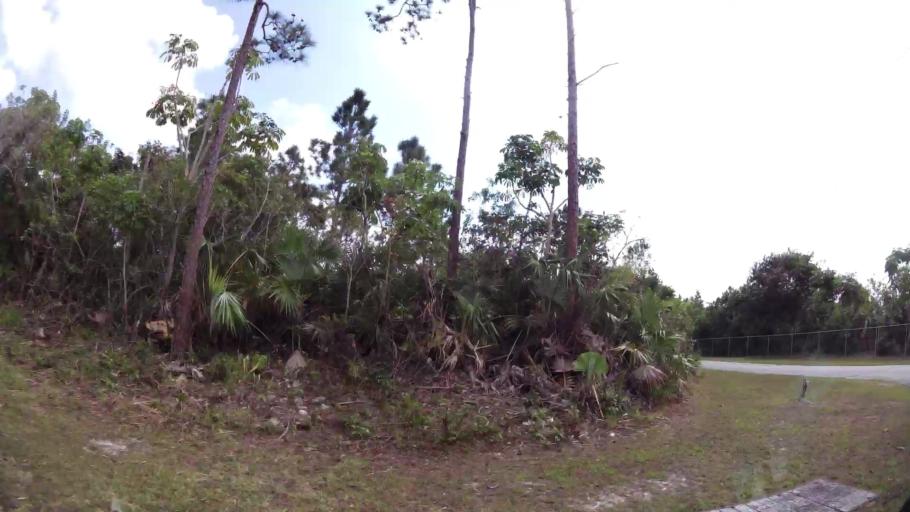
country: BS
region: Freeport
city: Freeport
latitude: 26.5151
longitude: -78.7088
